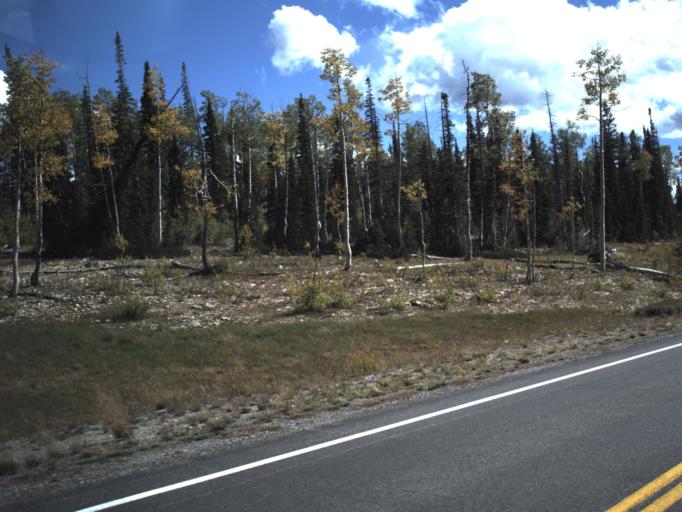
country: US
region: Utah
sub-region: Iron County
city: Parowan
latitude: 37.5481
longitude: -112.7860
